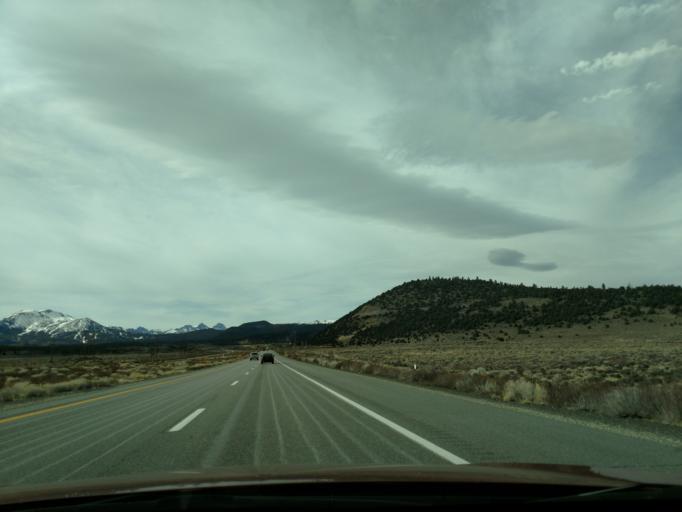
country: US
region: California
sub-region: Mono County
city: Mammoth Lakes
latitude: 37.6334
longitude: -118.8784
